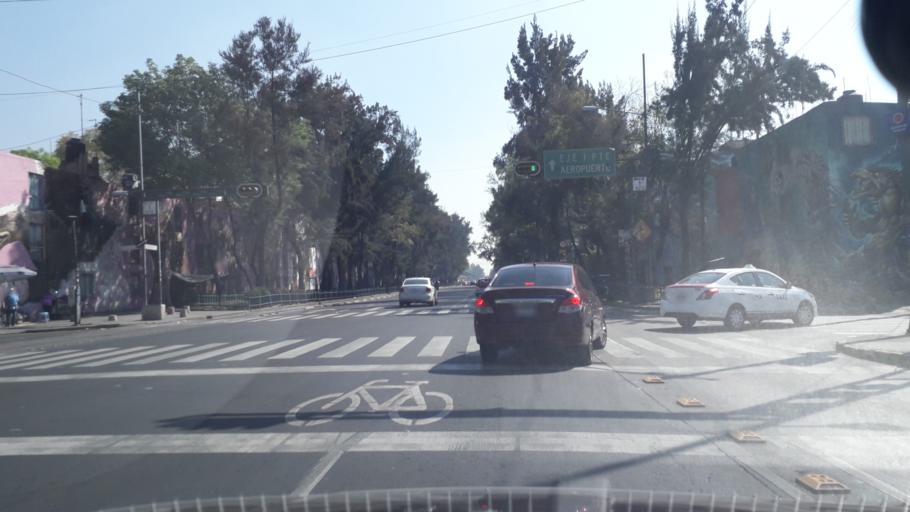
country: MX
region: Mexico City
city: Cuauhtemoc
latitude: 19.4458
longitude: -99.1507
